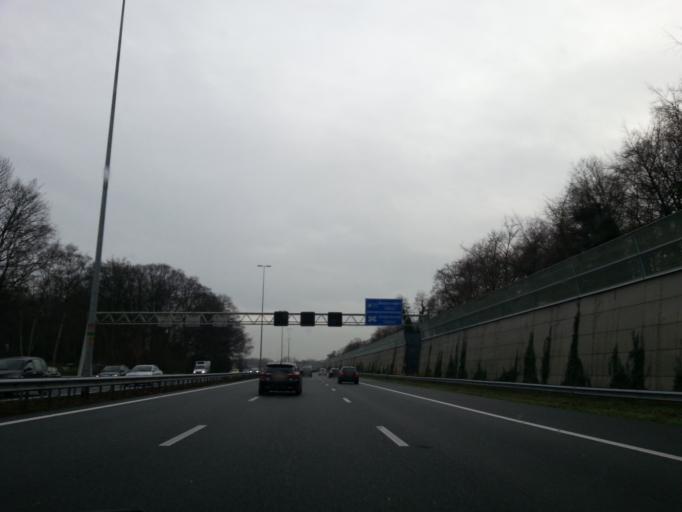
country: NL
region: Gelderland
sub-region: Gemeente Rozendaal
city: Rozendaal
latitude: 51.9982
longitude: 5.9516
